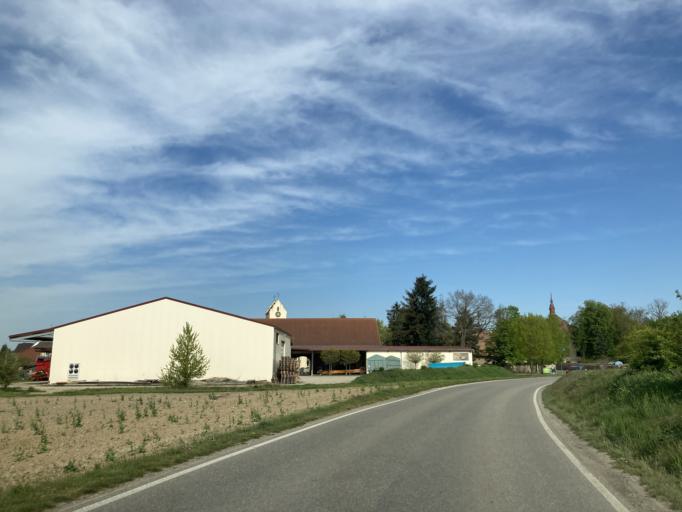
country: DE
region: Baden-Wuerttemberg
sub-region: Freiburg Region
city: Hartheim
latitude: 47.9350
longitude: 7.6519
